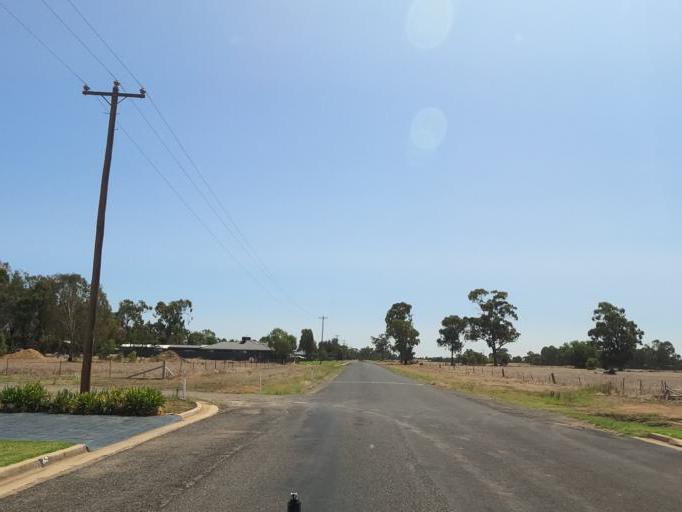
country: AU
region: New South Wales
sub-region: Corowa Shire
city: Mulwala
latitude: -35.9840
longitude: 146.0001
